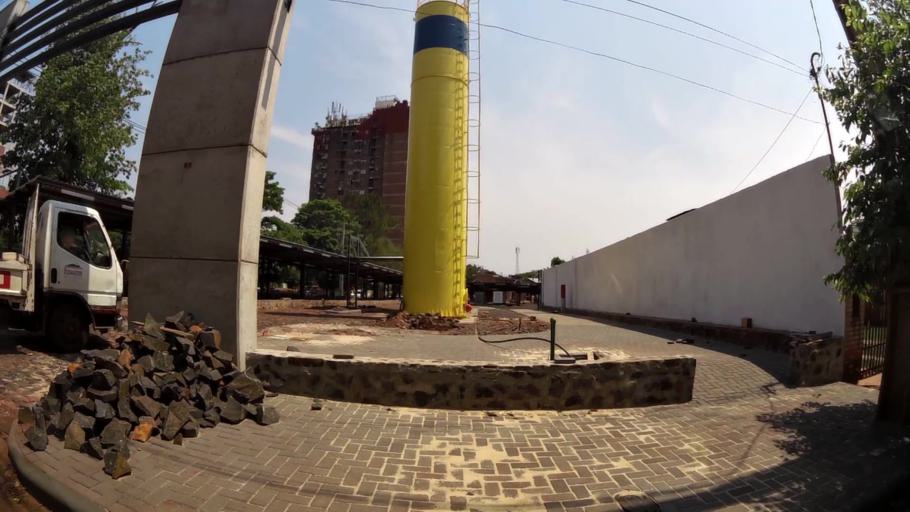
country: PY
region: Alto Parana
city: Ciudad del Este
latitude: -25.5158
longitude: -54.6127
